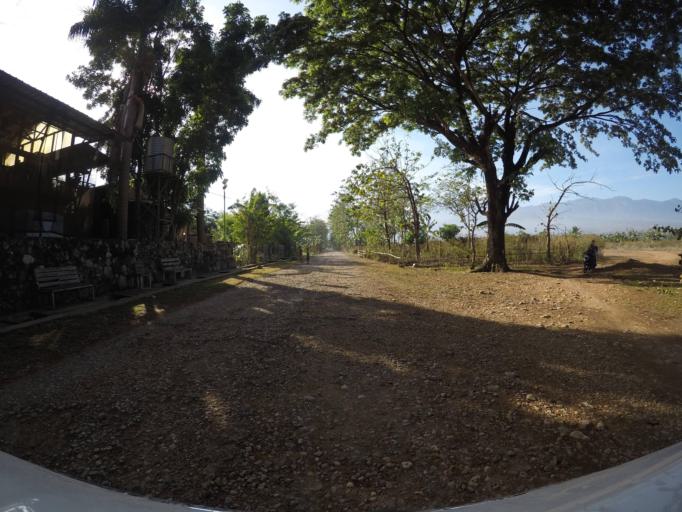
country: TL
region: Bobonaro
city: Maliana
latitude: -8.9702
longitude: 125.2124
